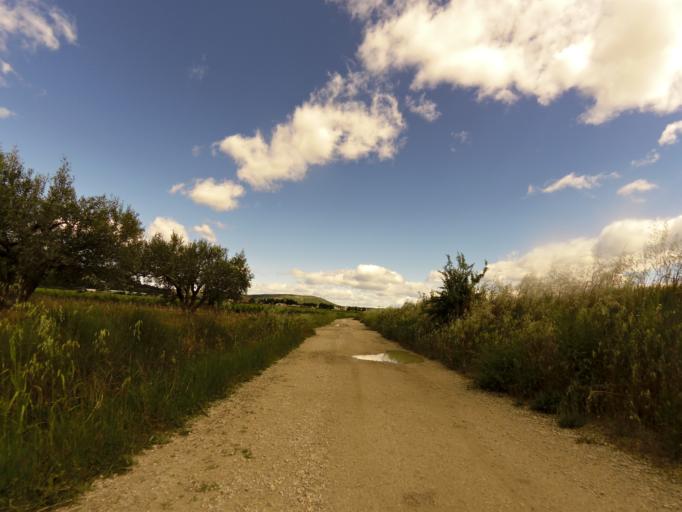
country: FR
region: Languedoc-Roussillon
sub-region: Departement du Gard
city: Calvisson
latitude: 43.7750
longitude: 4.2042
